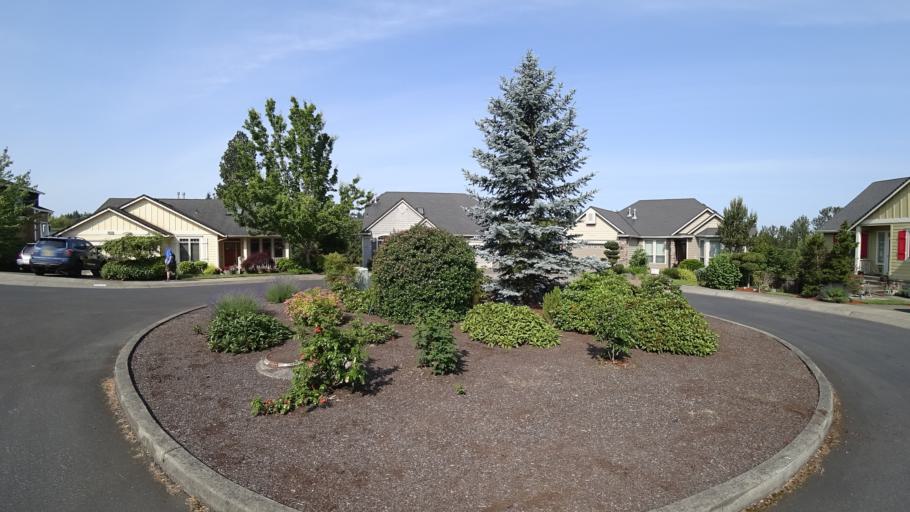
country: US
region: Oregon
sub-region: Clackamas County
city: Happy Valley
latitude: 45.4608
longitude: -122.5267
